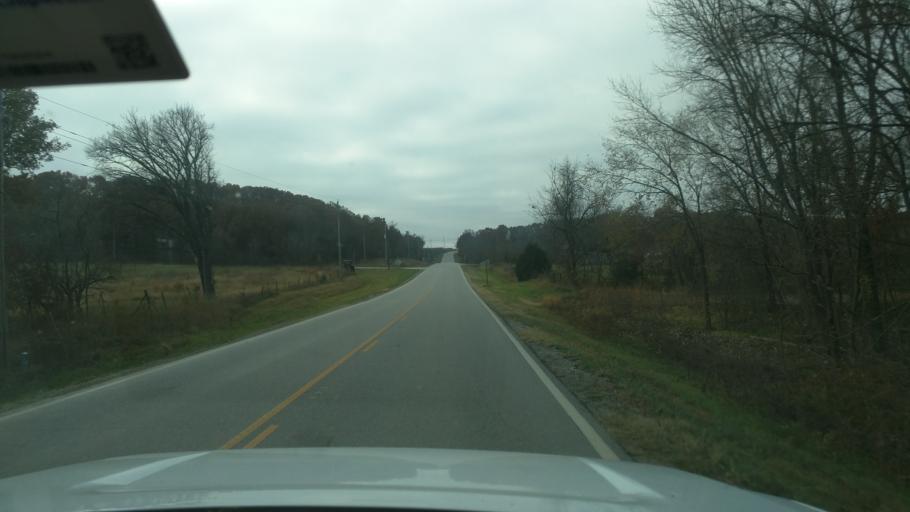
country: US
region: Kansas
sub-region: Greenwood County
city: Eureka
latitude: 37.7049
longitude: -96.2229
